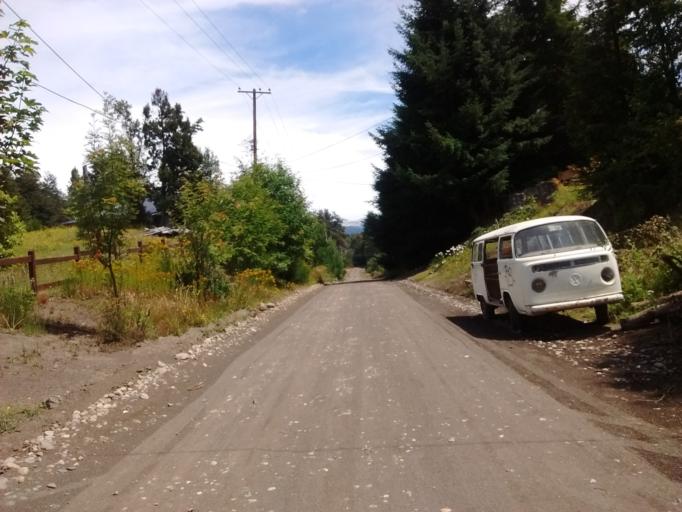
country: AR
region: Neuquen
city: Villa La Angostura
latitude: -40.7436
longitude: -71.6613
